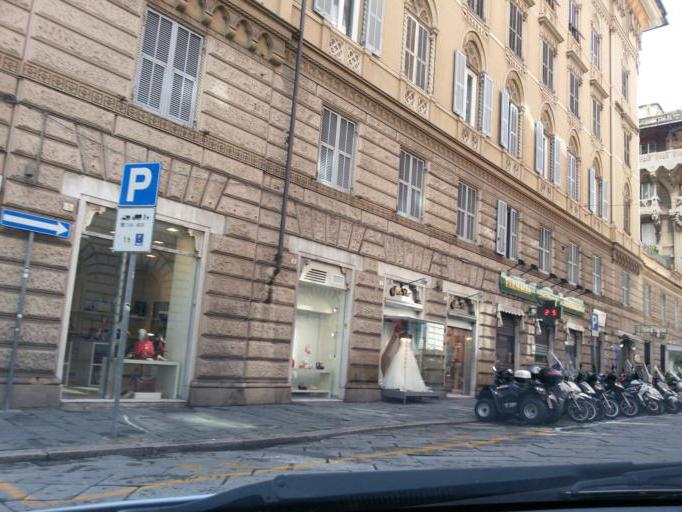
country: IT
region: Liguria
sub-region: Provincia di Genova
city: San Teodoro
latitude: 44.4055
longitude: 8.9413
